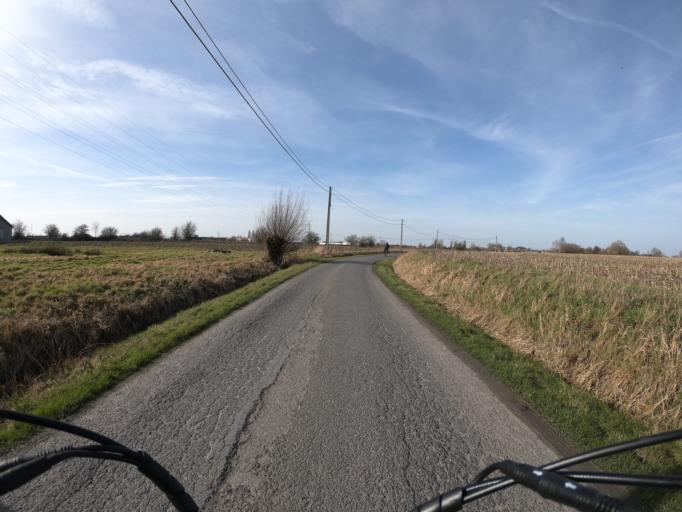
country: BE
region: Flanders
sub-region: Provincie West-Vlaanderen
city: Menen
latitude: 50.8210
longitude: 3.1265
